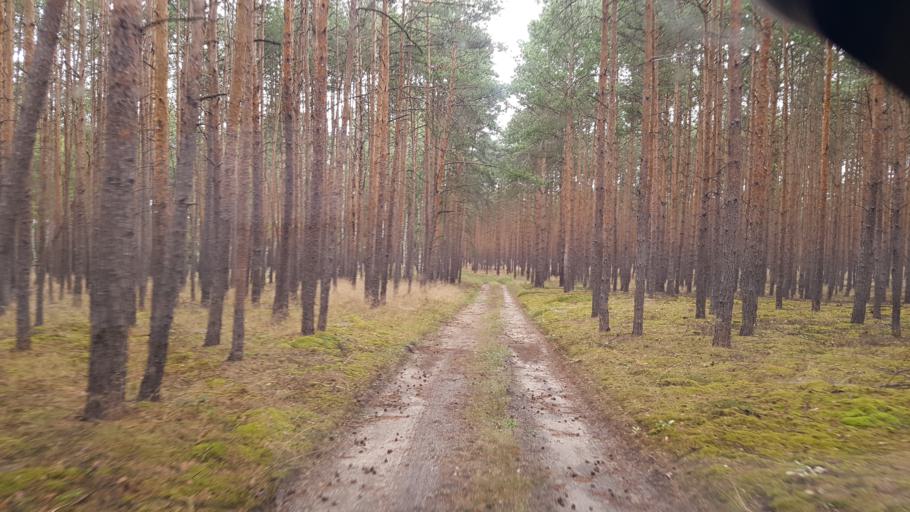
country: DE
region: Brandenburg
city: Schilda
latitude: 51.6412
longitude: 13.3466
